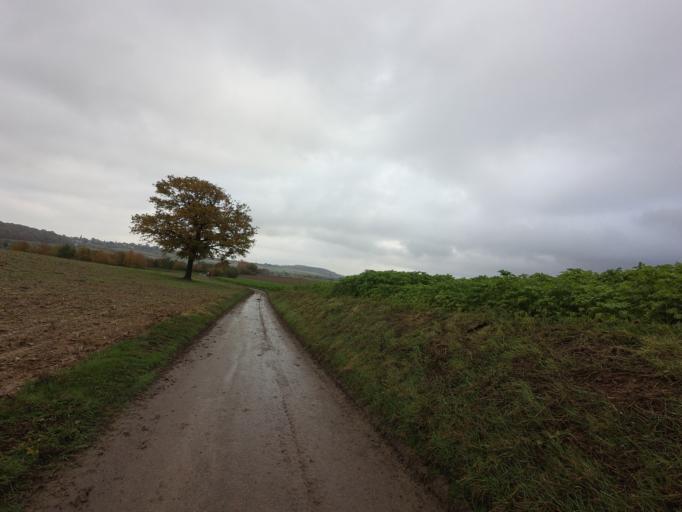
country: NL
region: Limburg
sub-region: Gemeente Simpelveld
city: Simpelveld
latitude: 50.7900
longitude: 5.9726
